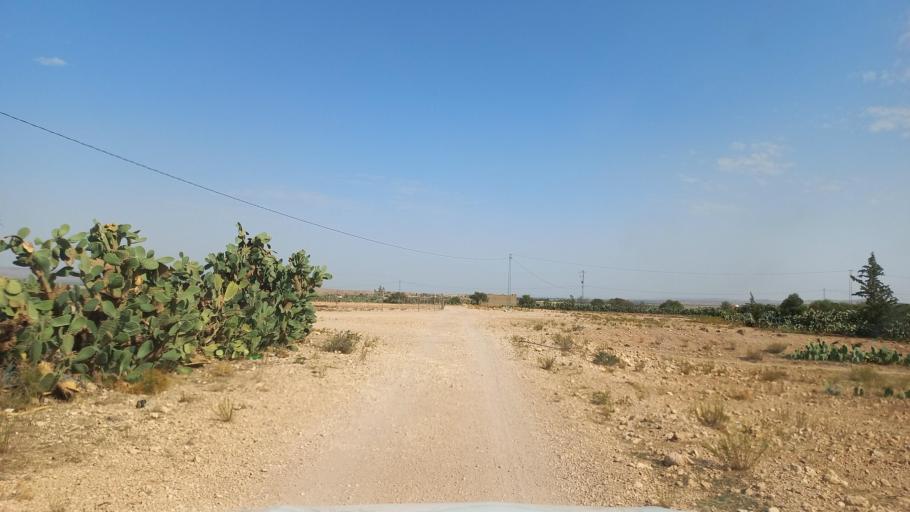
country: TN
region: Al Qasrayn
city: Kasserine
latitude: 35.2836
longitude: 8.9452
